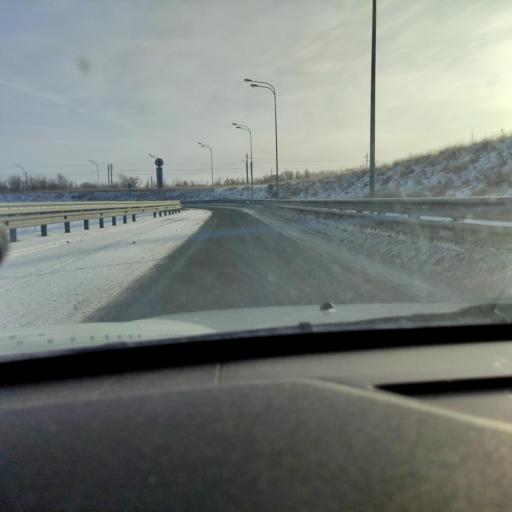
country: RU
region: Samara
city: Smyshlyayevka
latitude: 53.1482
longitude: 50.3798
